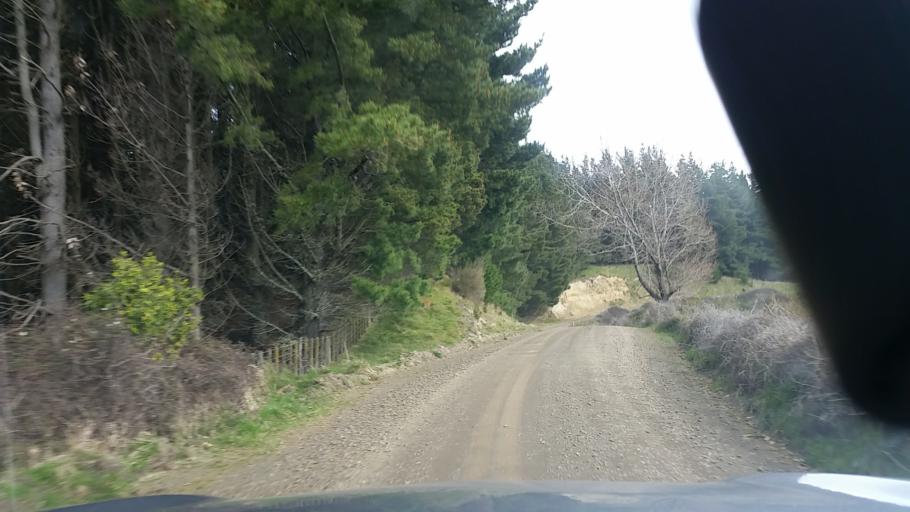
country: NZ
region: Hawke's Bay
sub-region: Napier City
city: Napier
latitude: -39.2284
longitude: 176.9859
